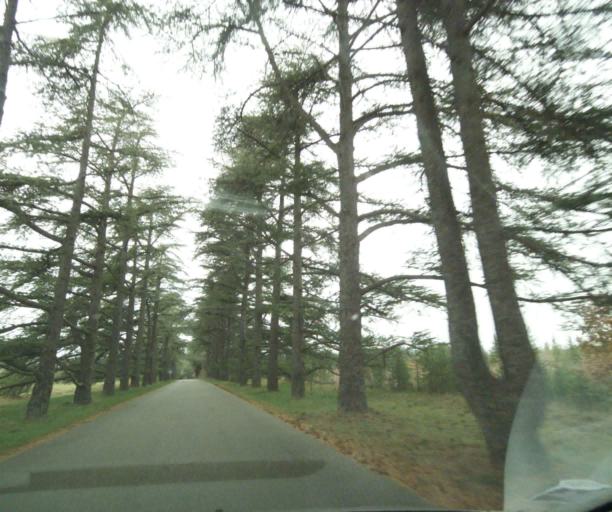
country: FR
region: Provence-Alpes-Cote d'Azur
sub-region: Departement du Var
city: Vinon-sur-Verdon
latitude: 43.7141
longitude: 5.7546
